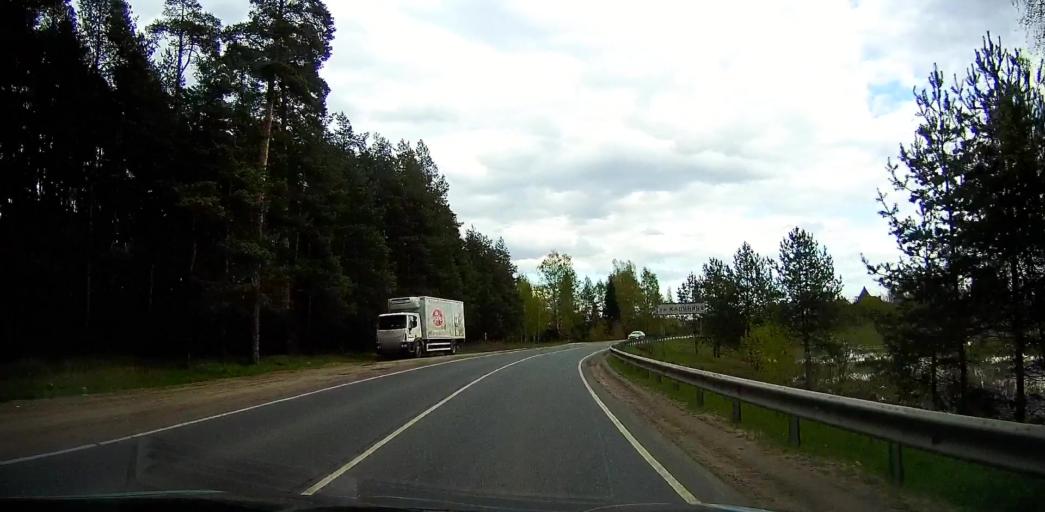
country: RU
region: Moskovskaya
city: Pavlovskiy Posad
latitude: 55.8023
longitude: 38.6771
